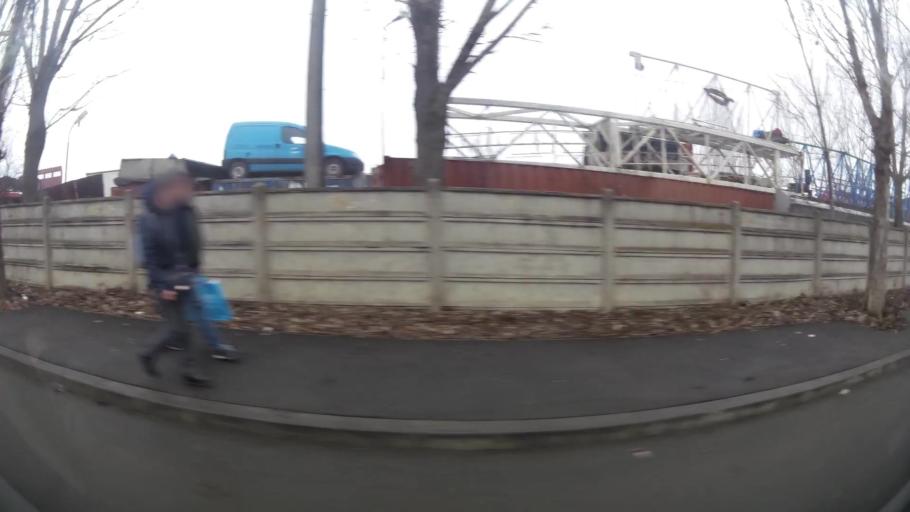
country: RO
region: Ilfov
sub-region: Comuna Chiajna
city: Rosu
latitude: 44.4760
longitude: 26.0085
